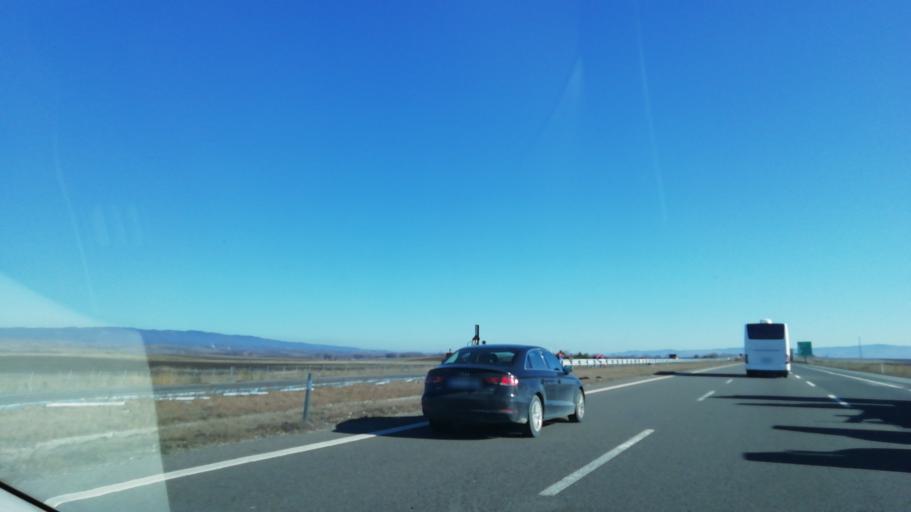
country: TR
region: Bolu
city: Dortdivan
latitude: 40.7467
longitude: 32.0971
